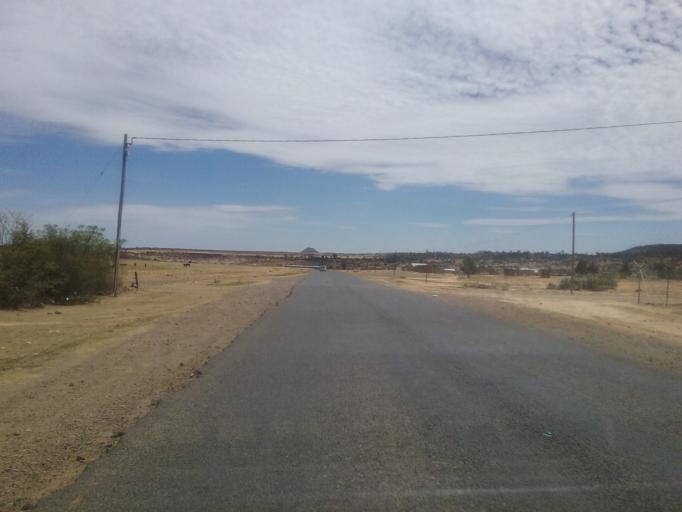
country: LS
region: Mafeteng
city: Mafeteng
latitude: -29.8568
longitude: 27.2337
